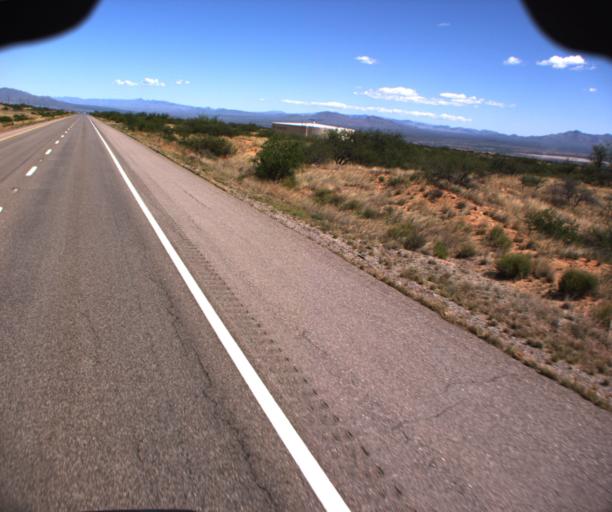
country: US
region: Arizona
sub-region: Cochise County
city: Whetstone
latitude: 31.9074
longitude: -110.3410
